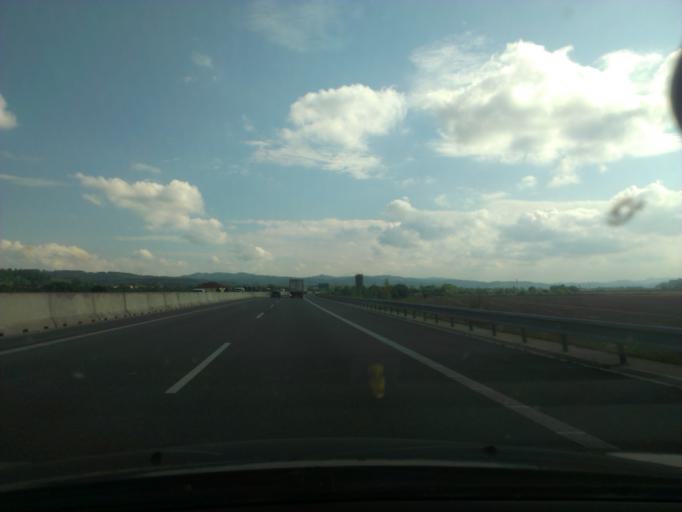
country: SK
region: Zilinsky
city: Bytca
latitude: 49.1995
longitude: 18.5193
